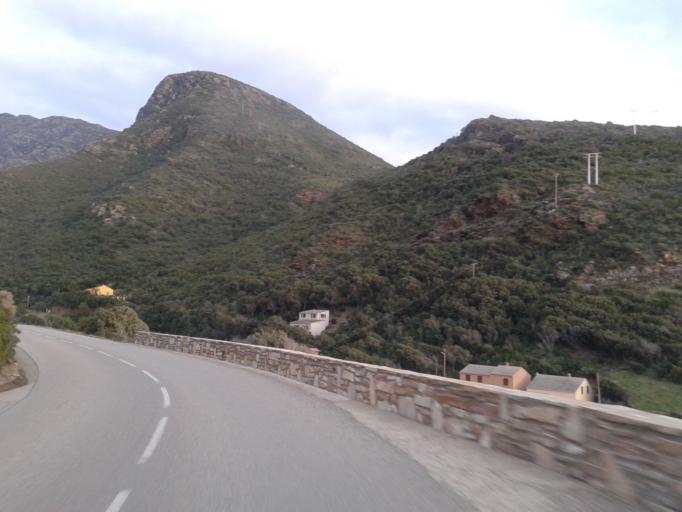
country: FR
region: Corsica
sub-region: Departement de la Haute-Corse
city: Saint-Florent
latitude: 42.7614
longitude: 9.3402
